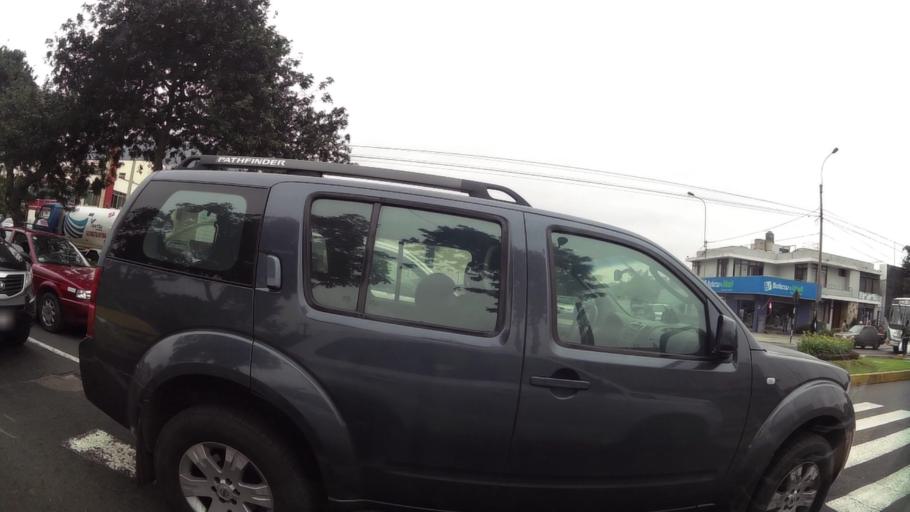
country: PE
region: Lima
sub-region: Lima
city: La Molina
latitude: -12.1094
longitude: -76.9714
